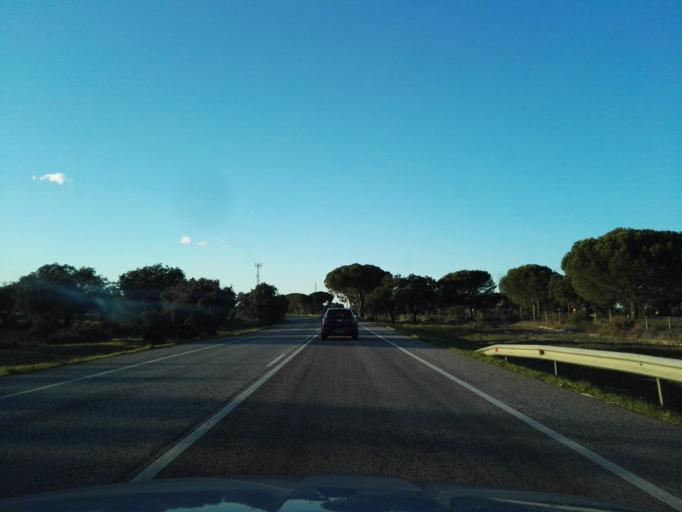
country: PT
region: Santarem
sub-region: Benavente
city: Poceirao
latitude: 38.8657
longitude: -8.7866
